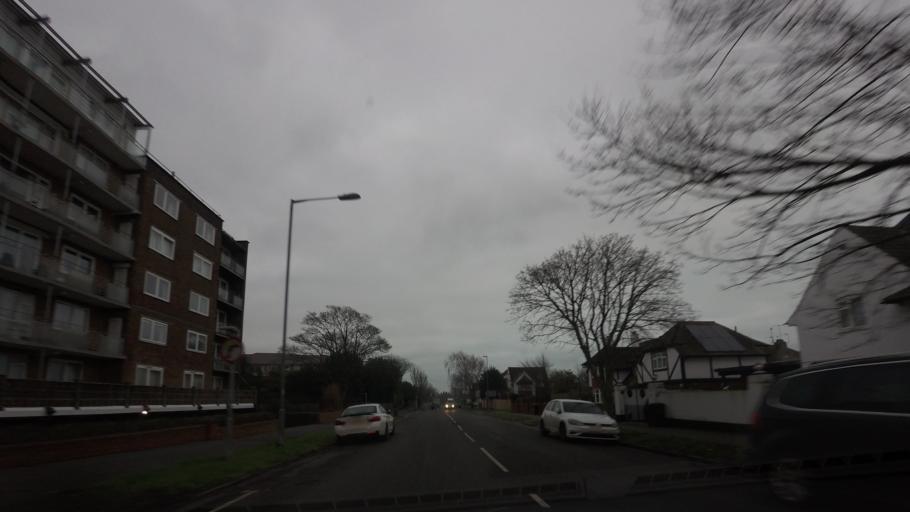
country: GB
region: England
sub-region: East Sussex
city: Bexhill-on-Sea
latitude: 50.8413
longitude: 0.4569
